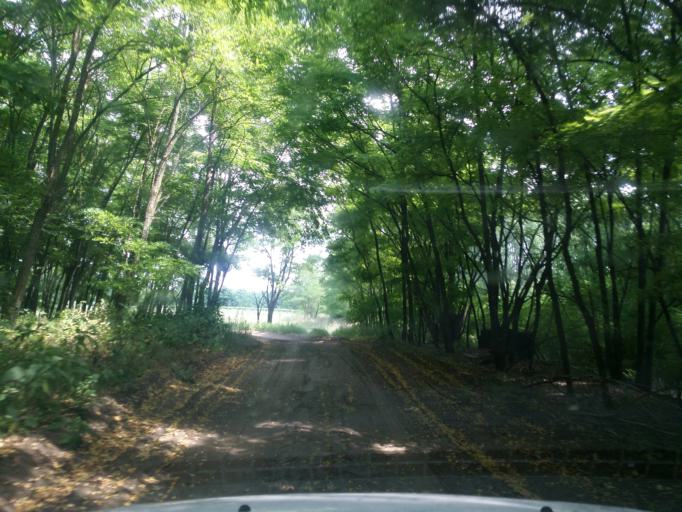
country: HU
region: Bacs-Kiskun
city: Jaszszentlaszlo
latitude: 46.6019
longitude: 19.7100
